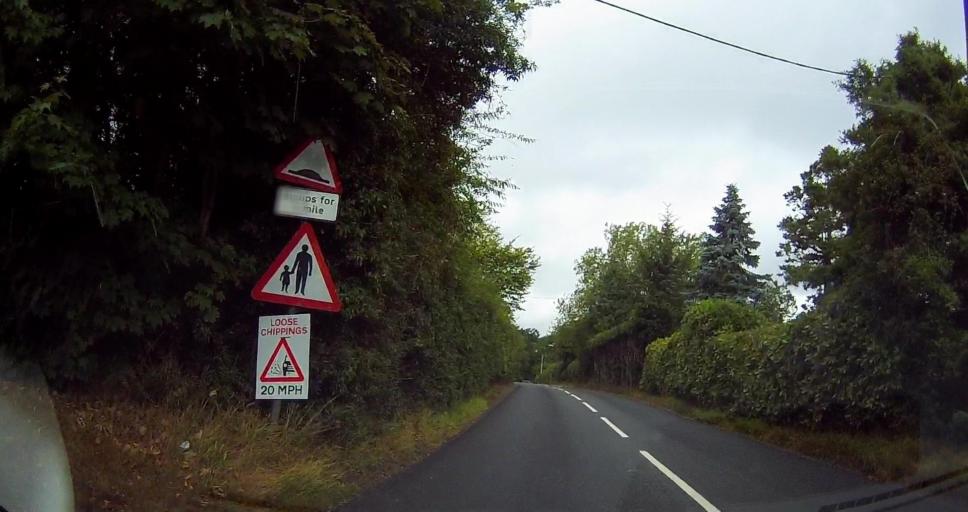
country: GB
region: England
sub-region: East Sussex
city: Wadhurst
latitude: 51.0945
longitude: 0.3906
